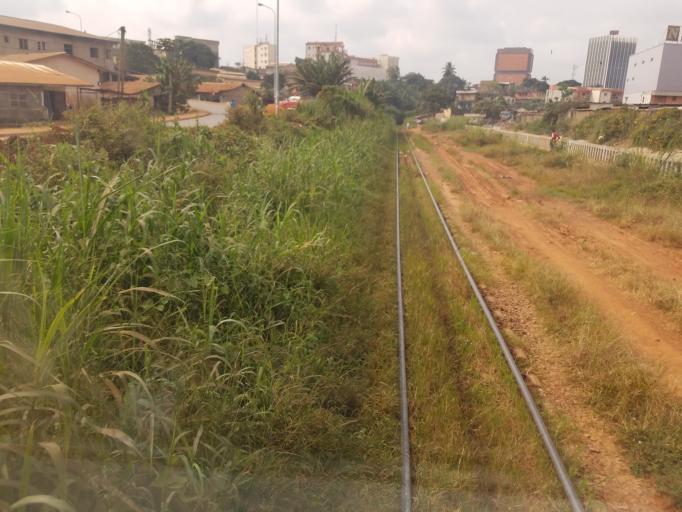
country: CM
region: Centre
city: Yaounde
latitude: 3.8650
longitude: 11.5248
